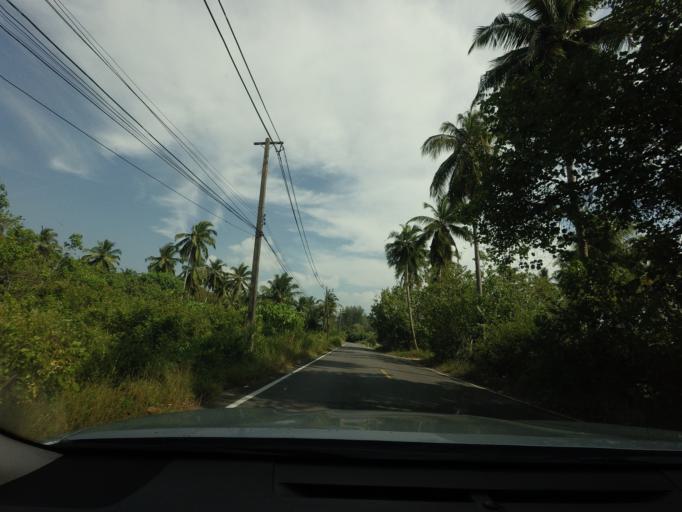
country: TH
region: Phangnga
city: Ban Khao Lak
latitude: 8.7283
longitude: 98.2362
